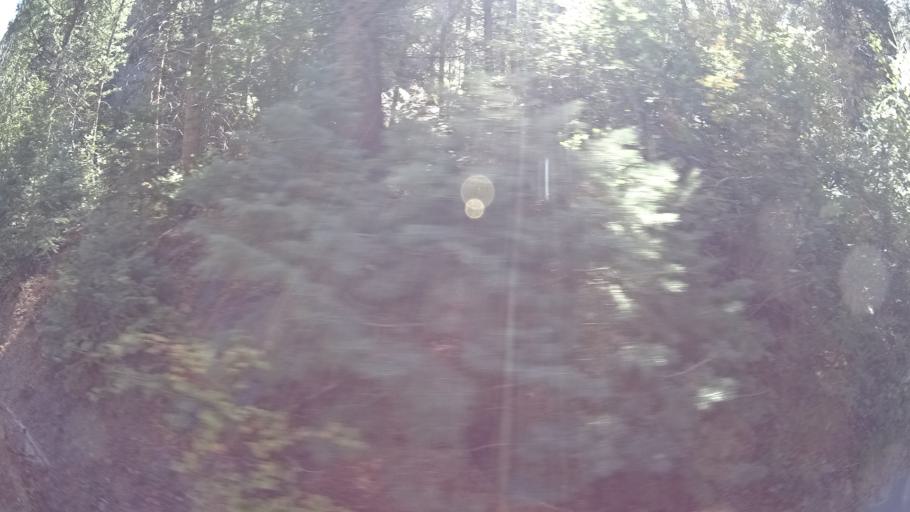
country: US
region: Colorado
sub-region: El Paso County
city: Colorado Springs
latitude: 38.7908
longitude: -104.8778
